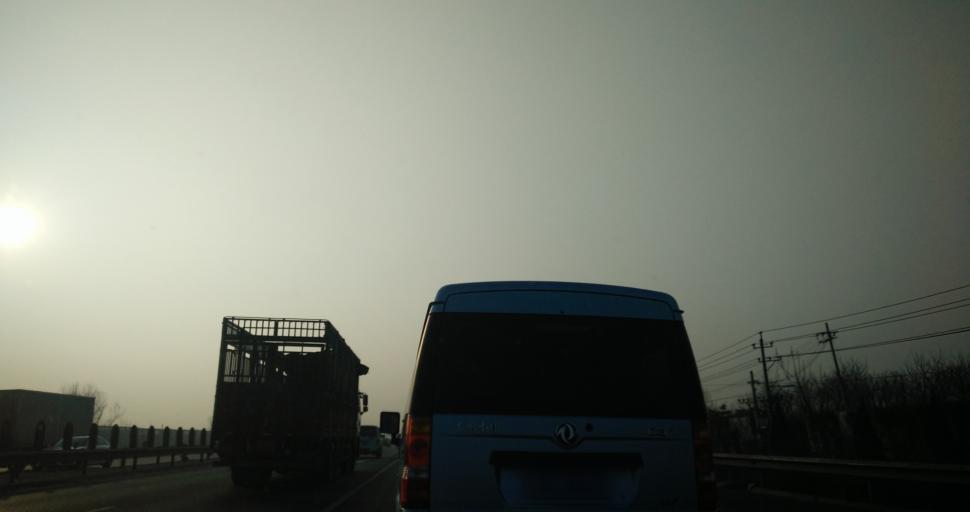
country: CN
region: Beijing
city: Yinghai
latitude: 39.7599
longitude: 116.3910
